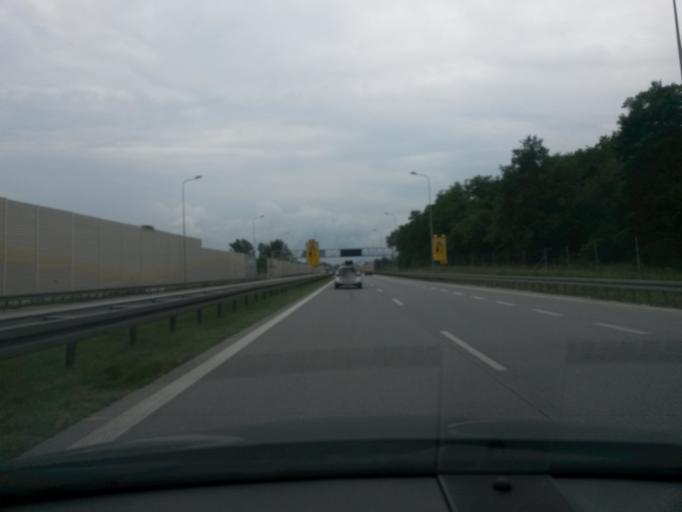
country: PL
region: Lodz Voivodeship
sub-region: Powiat skierniewicki
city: Kowiesy
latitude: 51.9247
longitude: 20.4616
